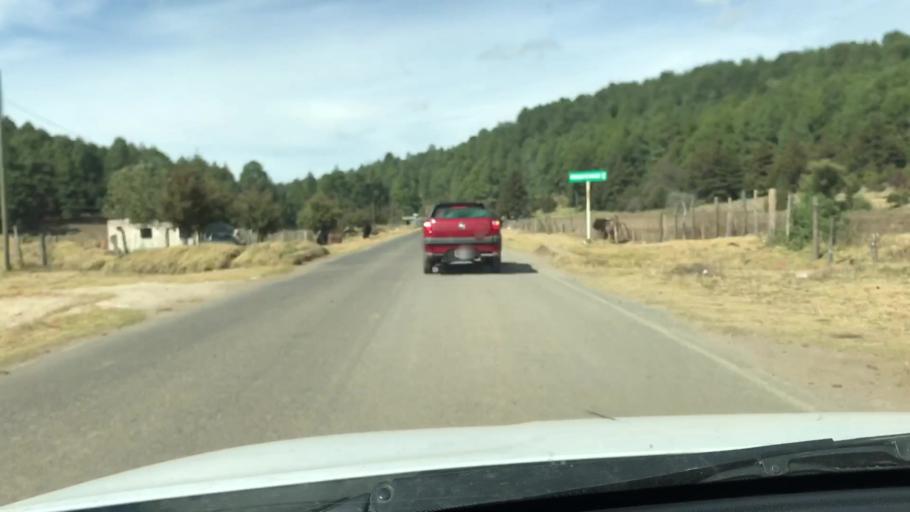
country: MX
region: Jalisco
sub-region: Amacueca
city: Tepec
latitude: 20.0393
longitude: -103.6906
